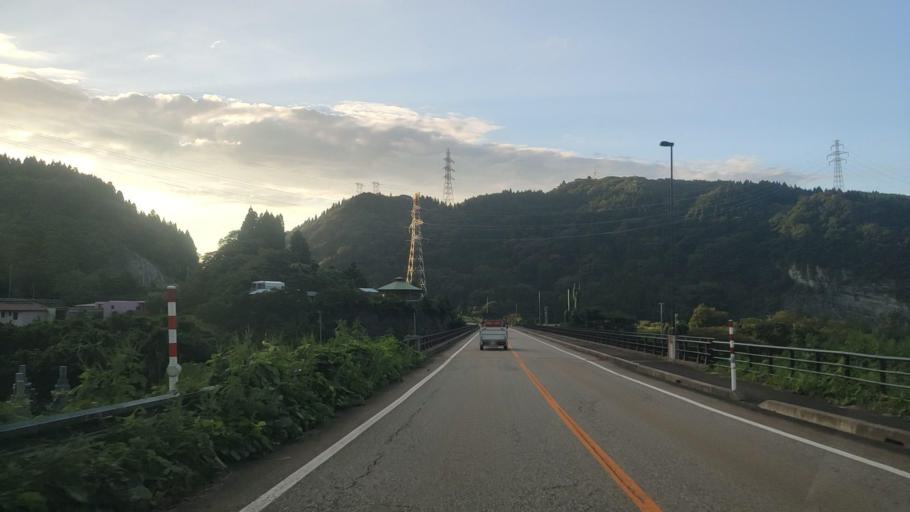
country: JP
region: Toyama
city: Nanto-shi
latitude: 36.5624
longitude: 137.0066
